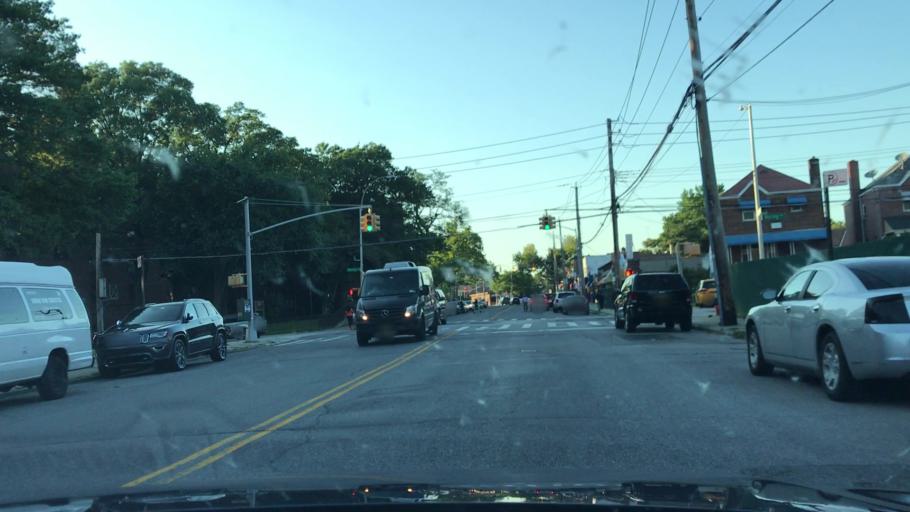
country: US
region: New York
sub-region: Bronx
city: The Bronx
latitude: 40.8607
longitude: -73.8575
